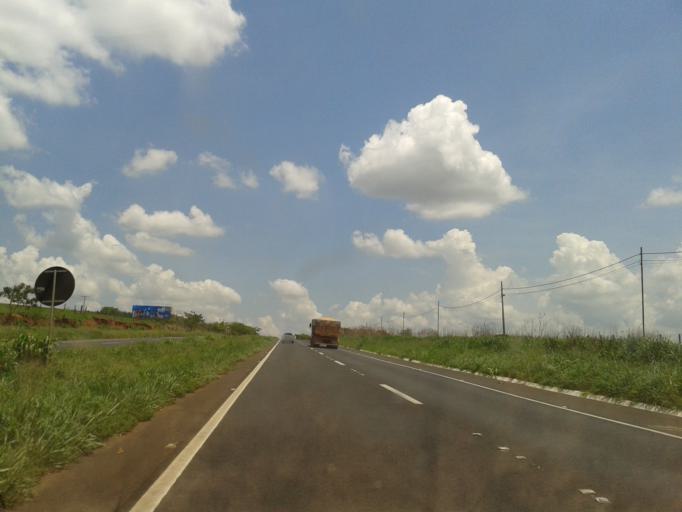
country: BR
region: Minas Gerais
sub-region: Uberlandia
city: Uberlandia
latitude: -18.8999
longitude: -48.3668
